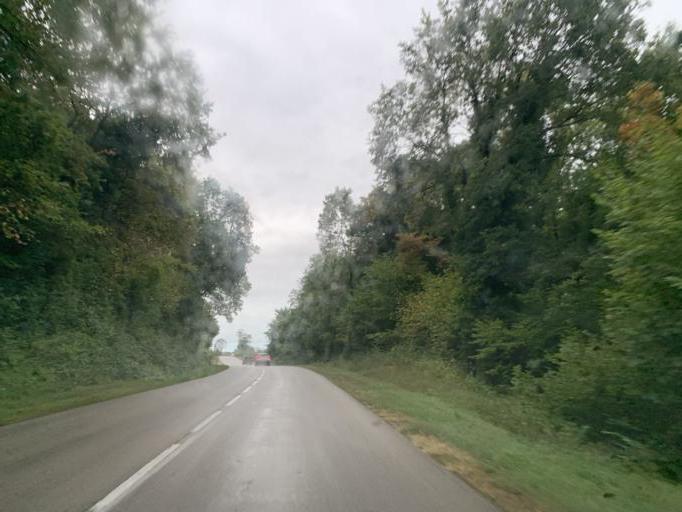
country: FR
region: Rhone-Alpes
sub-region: Departement de l'Ain
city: Villebois
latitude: 45.8213
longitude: 5.4475
